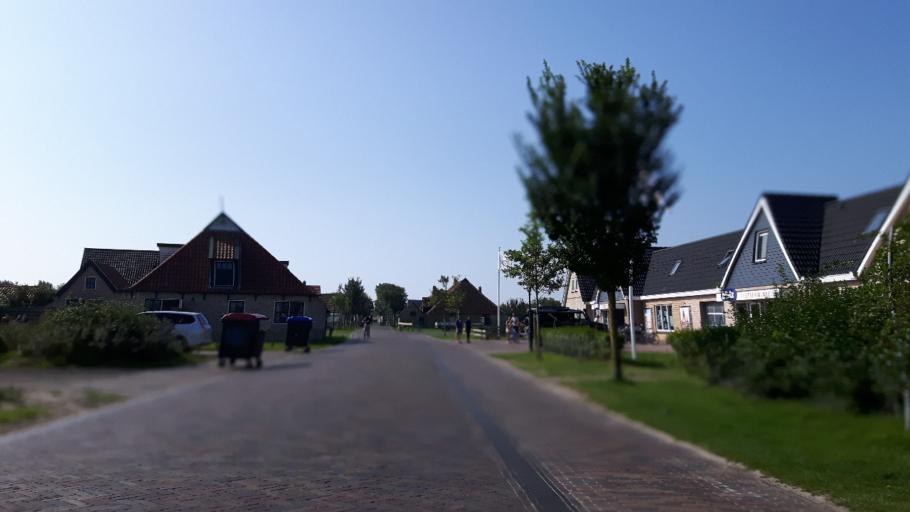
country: NL
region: Friesland
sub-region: Gemeente Ameland
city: Nes
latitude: 53.4512
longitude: 5.8012
